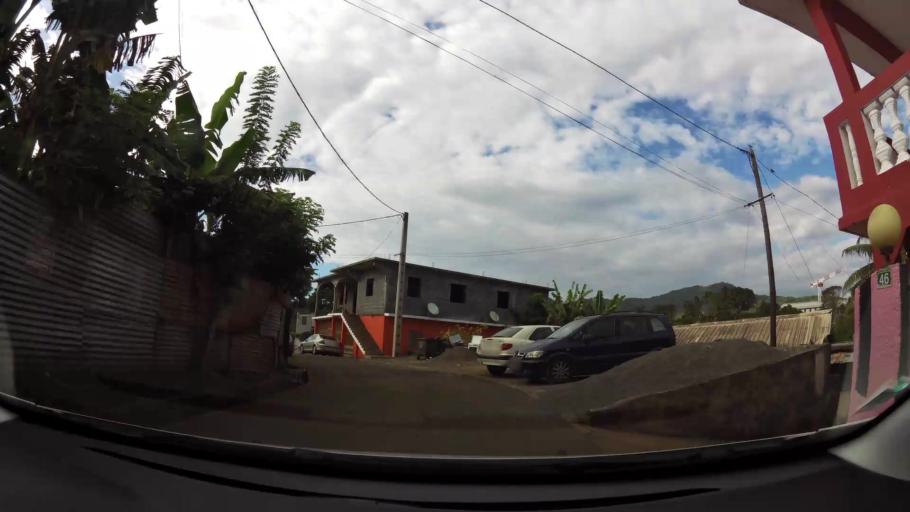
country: YT
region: Ouangani
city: Ouangani
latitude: -12.8384
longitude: 45.1297
